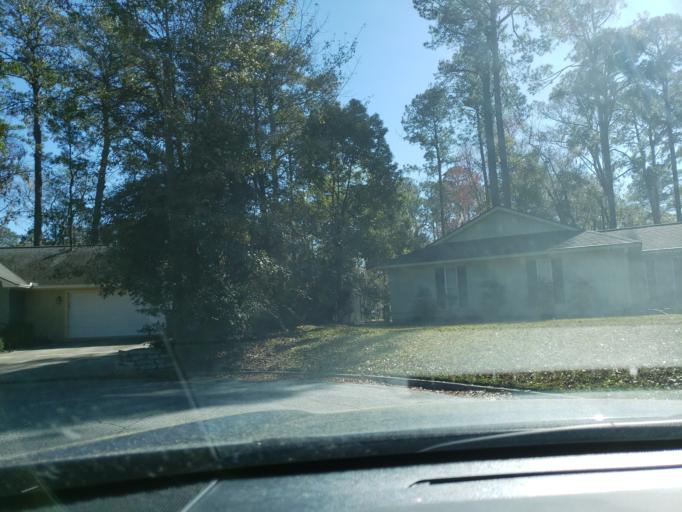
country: US
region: Georgia
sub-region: Chatham County
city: Isle of Hope
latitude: 31.9841
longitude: -81.0616
